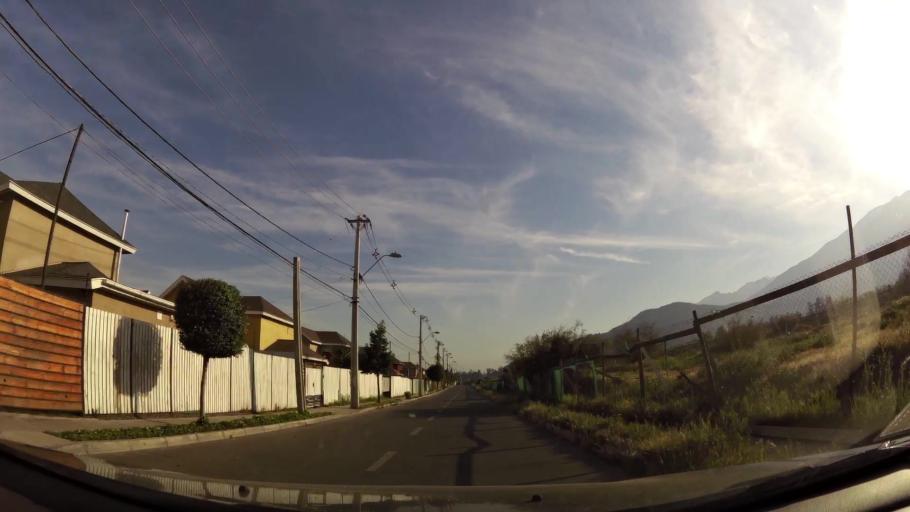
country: CL
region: Santiago Metropolitan
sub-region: Provincia de Cordillera
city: Puente Alto
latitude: -33.5657
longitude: -70.5438
